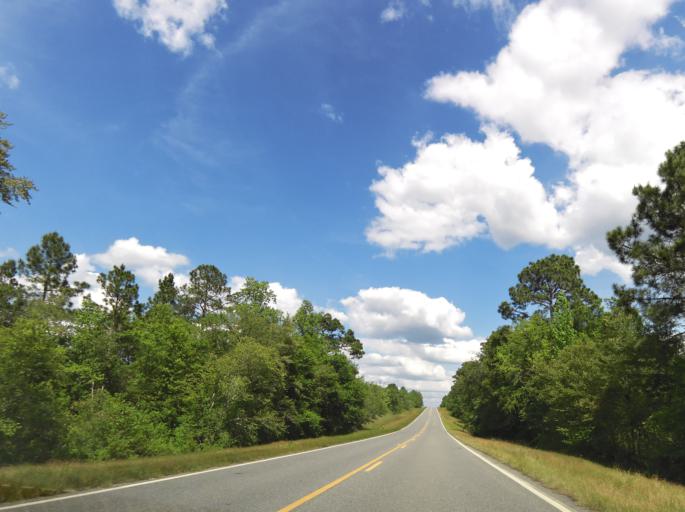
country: US
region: Georgia
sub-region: Wheeler County
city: Alamo
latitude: 32.2609
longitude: -82.8060
